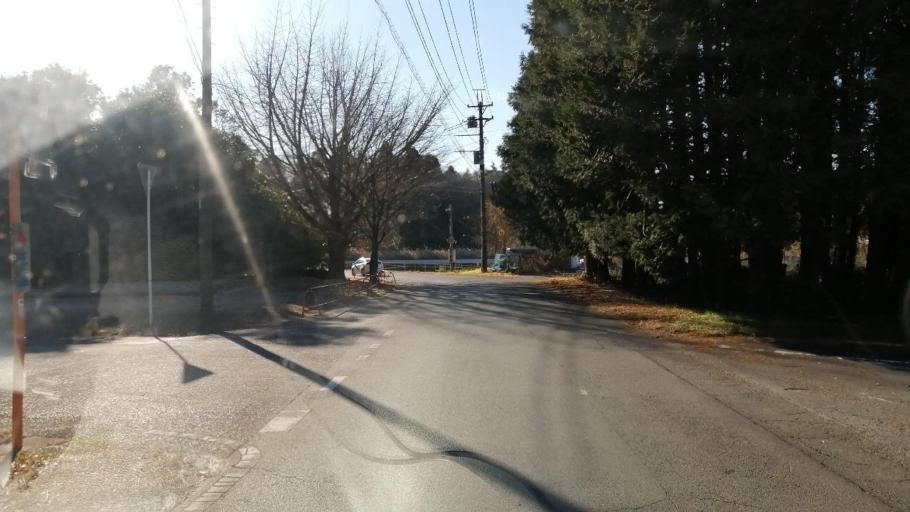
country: JP
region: Chiba
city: Narita
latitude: 35.7735
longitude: 140.3633
